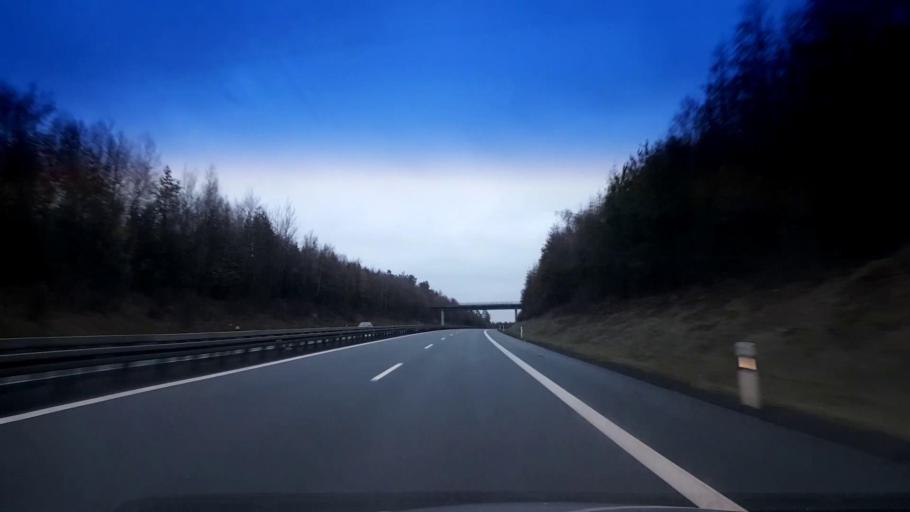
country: DE
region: Bavaria
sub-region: Upper Palatinate
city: Wiesau
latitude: 49.8978
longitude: 12.2205
